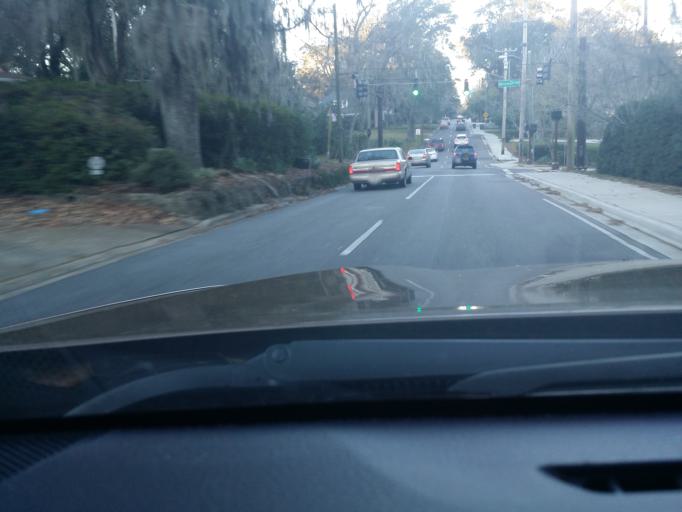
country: US
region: Florida
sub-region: Leon County
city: Tallahassee
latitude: 30.4573
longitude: -84.2676
